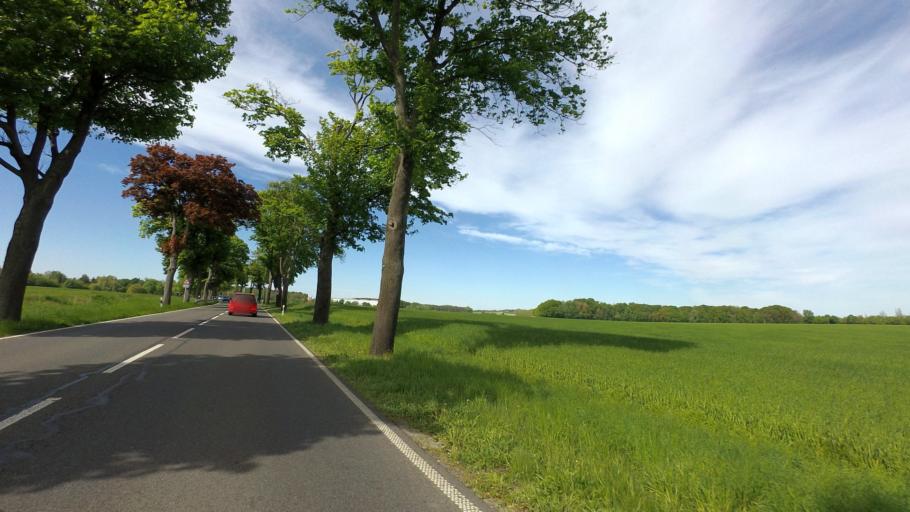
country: DE
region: Brandenburg
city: Rangsdorf
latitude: 52.2836
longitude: 13.4629
